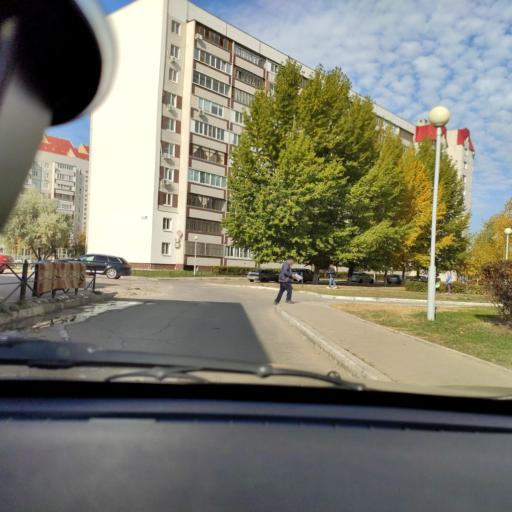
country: RU
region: Samara
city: Tol'yatti
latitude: 53.5445
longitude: 49.3685
